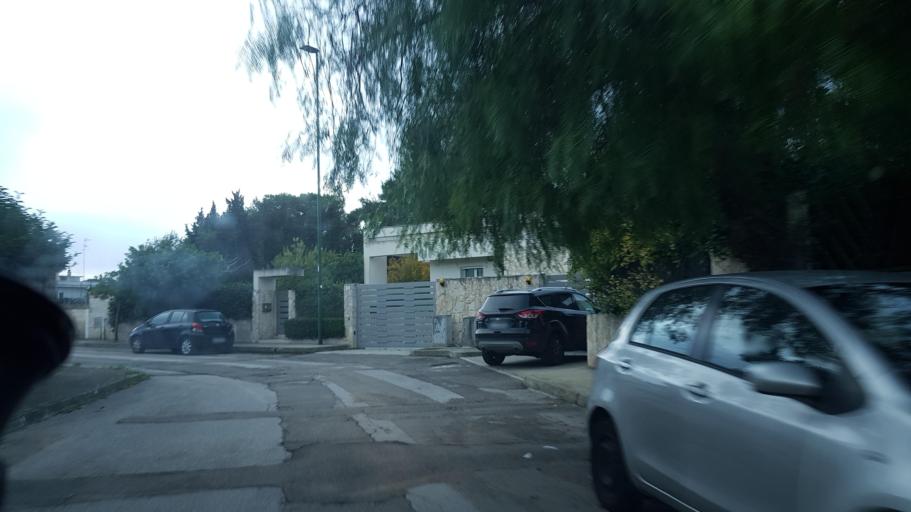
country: IT
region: Apulia
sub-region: Provincia di Lecce
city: Merine
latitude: 40.3401
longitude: 18.2171
